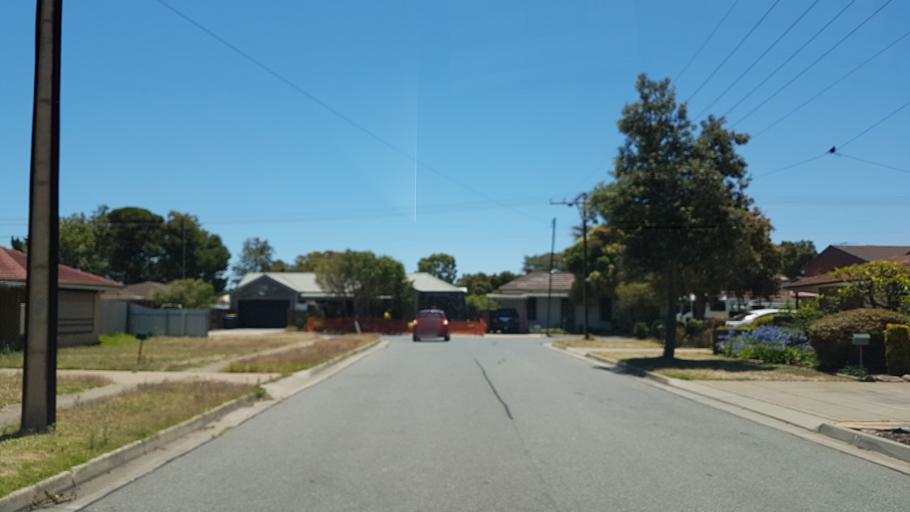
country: AU
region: South Australia
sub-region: Charles Sturt
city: West Lakes Shore
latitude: -34.8536
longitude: 138.4852
